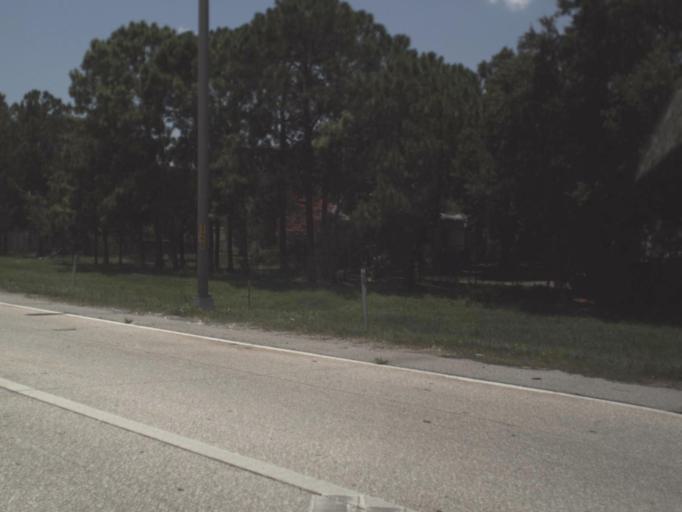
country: US
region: Florida
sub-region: Pinellas County
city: Lealman
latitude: 27.8041
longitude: -82.6629
